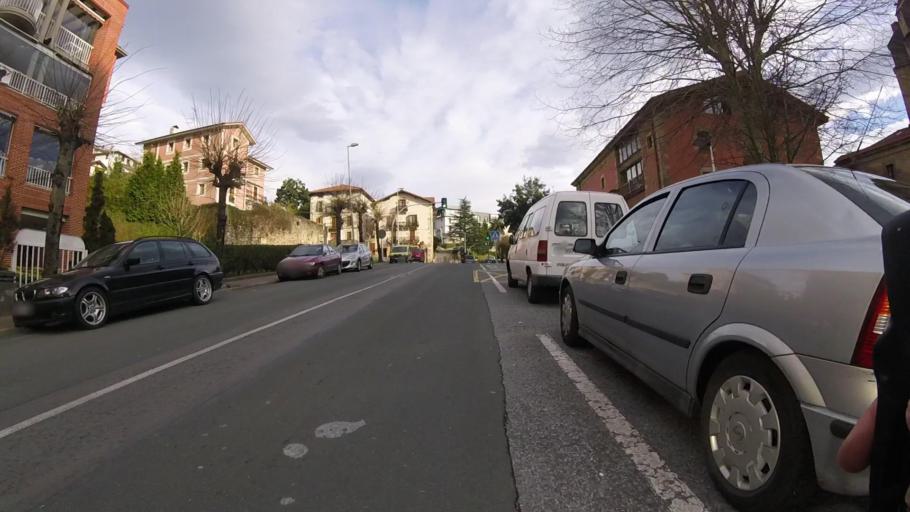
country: ES
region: Basque Country
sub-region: Provincia de Guipuzcoa
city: Lezo
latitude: 43.3003
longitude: -1.8606
